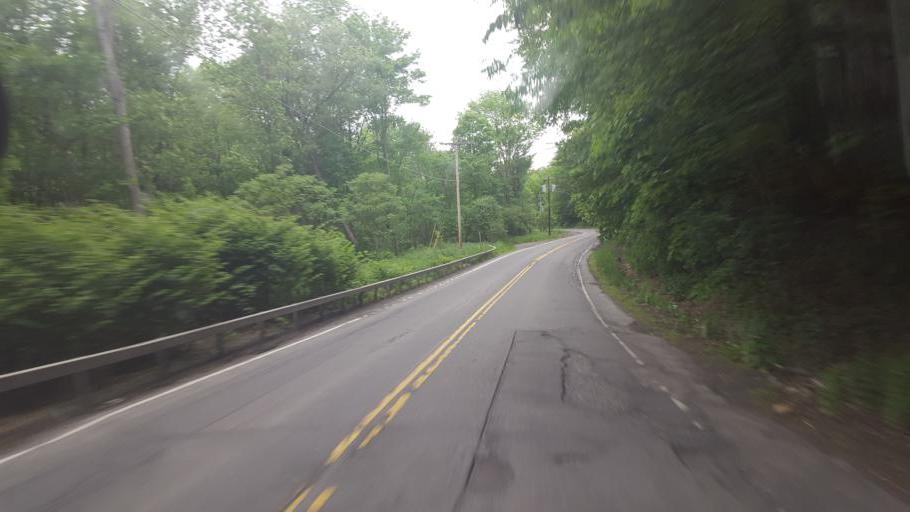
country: US
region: New York
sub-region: Herkimer County
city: Mohawk
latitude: 42.9917
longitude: -75.0011
